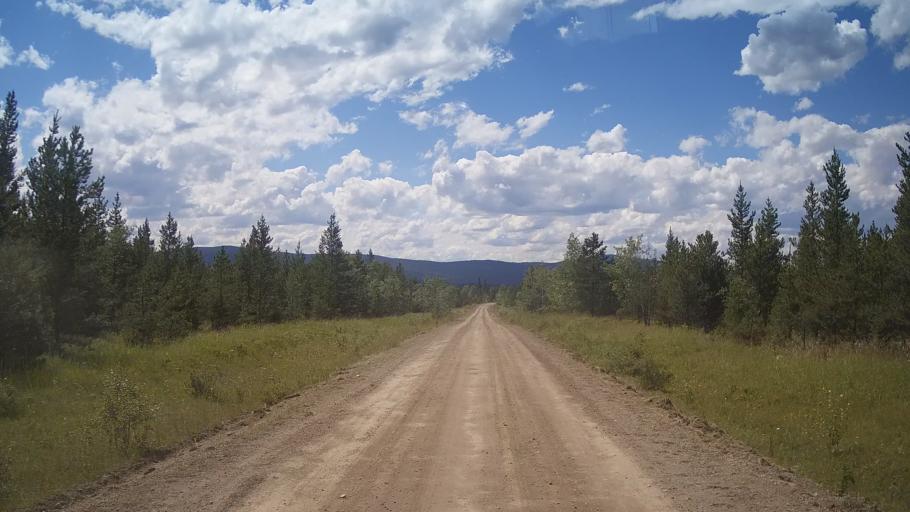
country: CA
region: British Columbia
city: Lillooet
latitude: 51.3406
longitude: -121.9367
